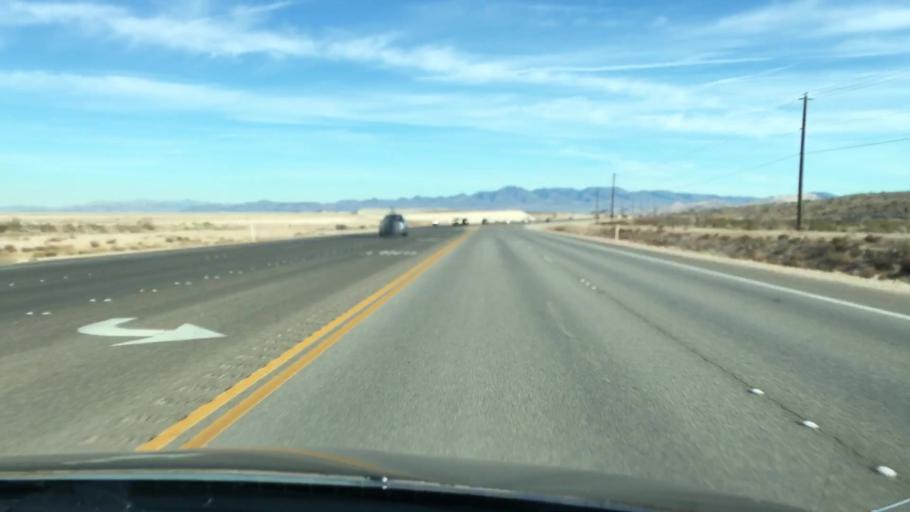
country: US
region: Nevada
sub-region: Clark County
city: Enterprise
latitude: 36.0288
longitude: -115.3280
